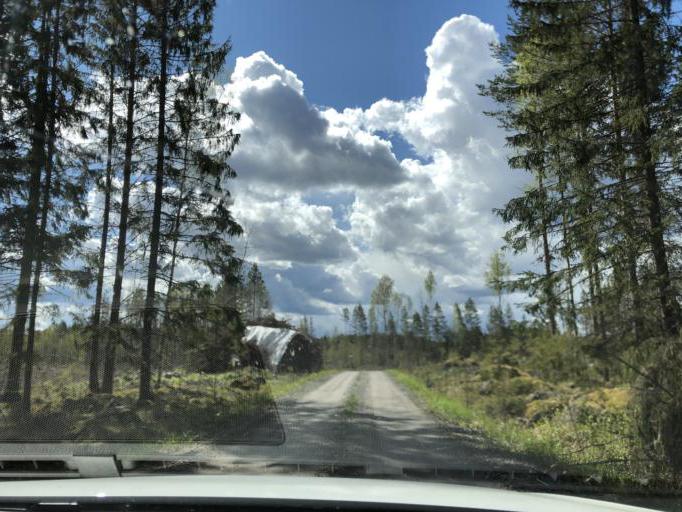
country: SE
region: Uppsala
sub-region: Heby Kommun
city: Tarnsjo
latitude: 60.2482
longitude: 16.9000
